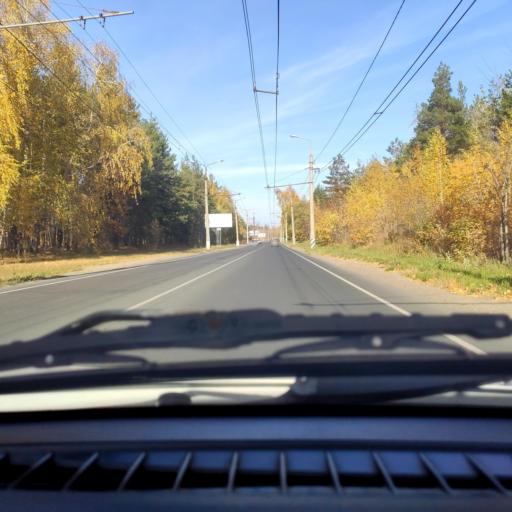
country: RU
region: Samara
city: Tol'yatti
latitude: 53.4911
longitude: 49.3853
